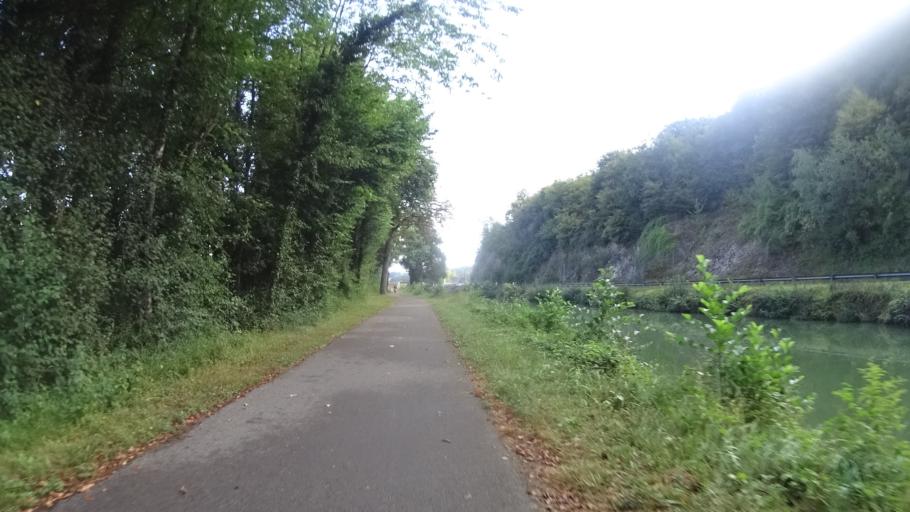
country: FR
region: Franche-Comte
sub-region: Departement du Doubs
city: Boussieres
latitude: 47.1533
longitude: 5.8559
